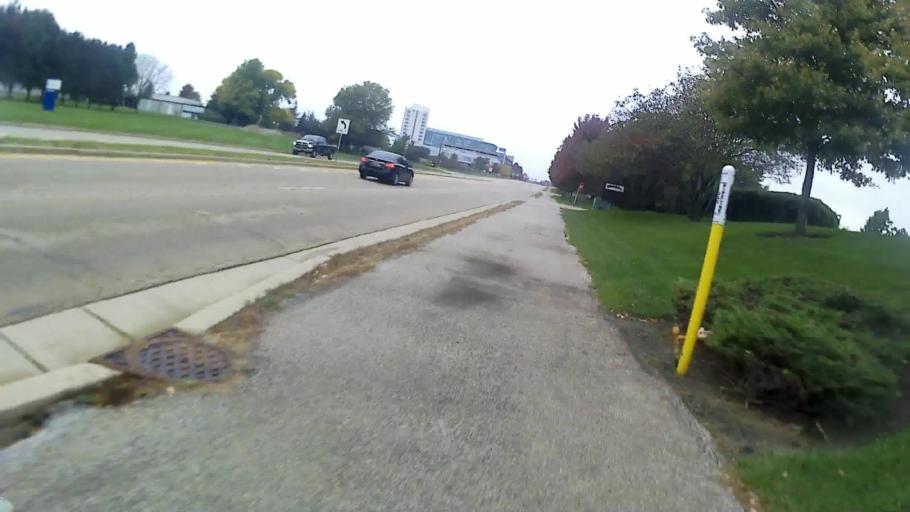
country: US
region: Illinois
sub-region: DuPage County
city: Warrenville
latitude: 41.8085
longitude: -88.1961
